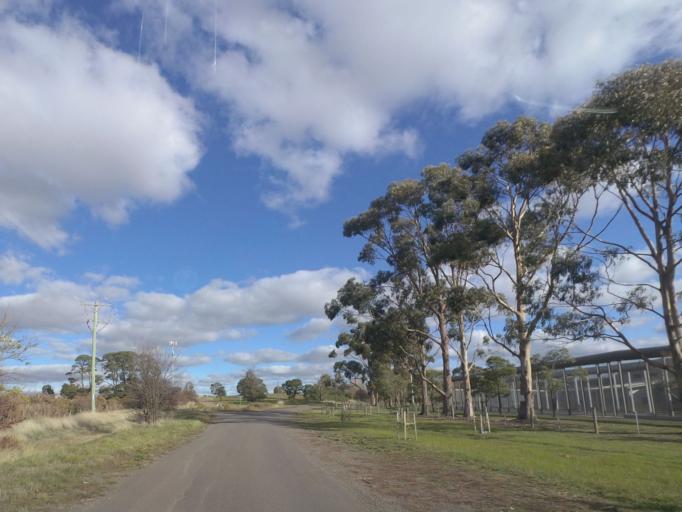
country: AU
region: Victoria
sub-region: Mount Alexander
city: Castlemaine
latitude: -37.1884
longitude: 144.3991
